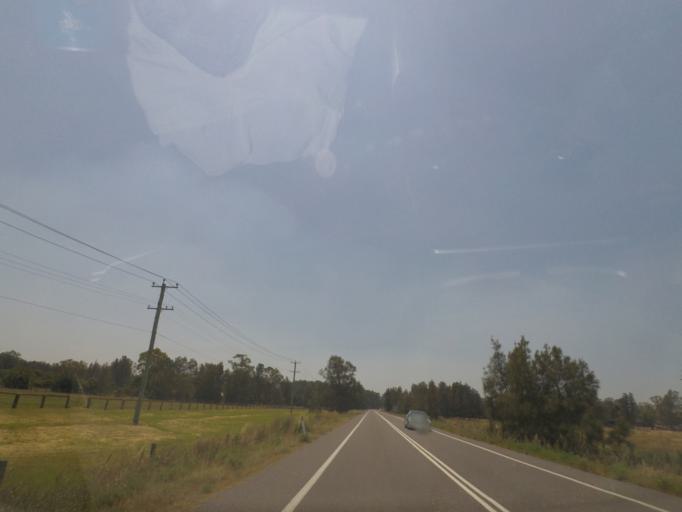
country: AU
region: New South Wales
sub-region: Port Stephens Shire
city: Medowie
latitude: -32.8052
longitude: 151.8779
